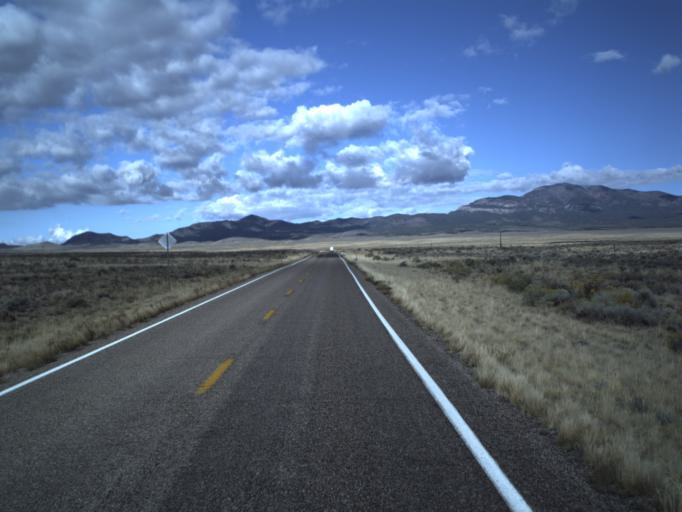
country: US
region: Utah
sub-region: Beaver County
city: Milford
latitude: 38.4344
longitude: -113.1361
